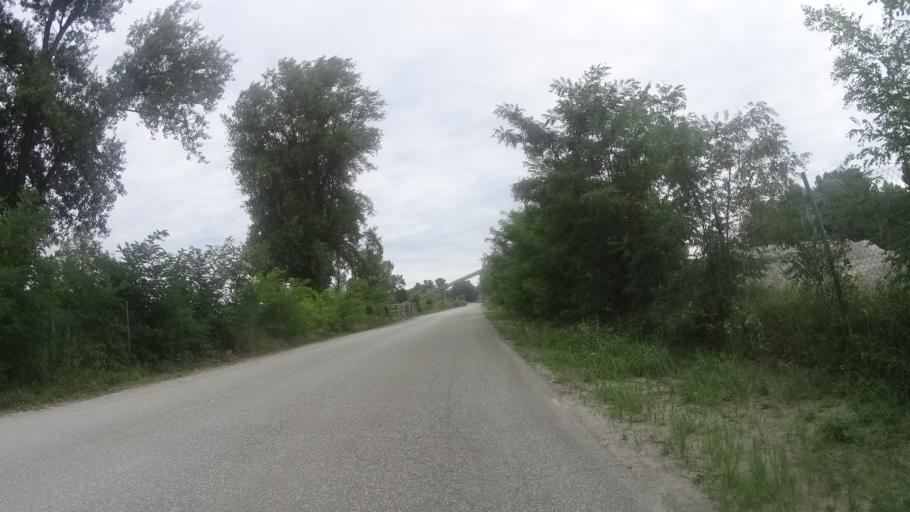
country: FR
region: Alsace
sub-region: Departement du Bas-Rhin
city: Seltz
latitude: 48.8931
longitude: 8.1350
